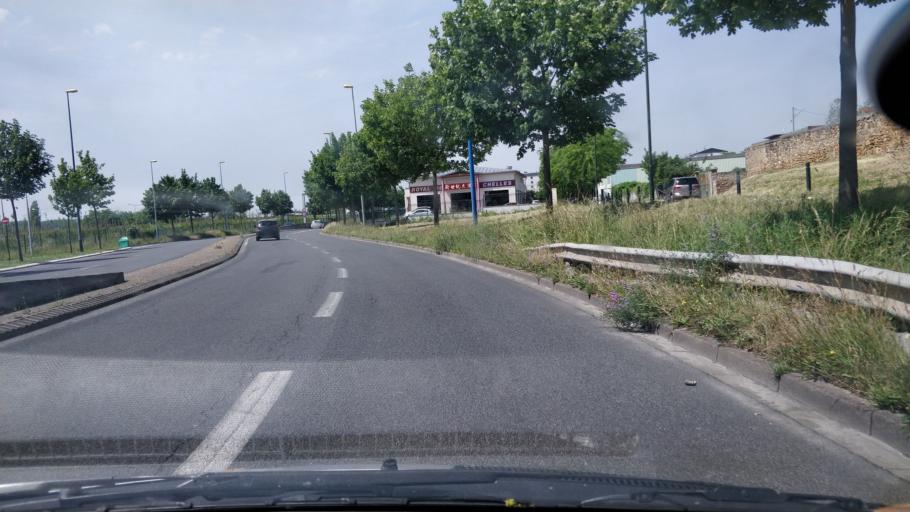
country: FR
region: Ile-de-France
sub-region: Departement de Seine-et-Marne
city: Chelles
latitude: 48.8775
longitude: 2.6059
